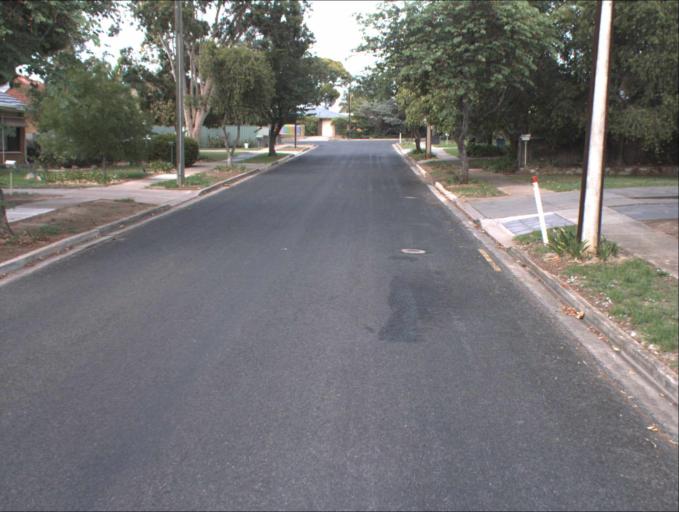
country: AU
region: South Australia
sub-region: Port Adelaide Enfield
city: Klemzig
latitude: -34.8822
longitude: 138.6310
